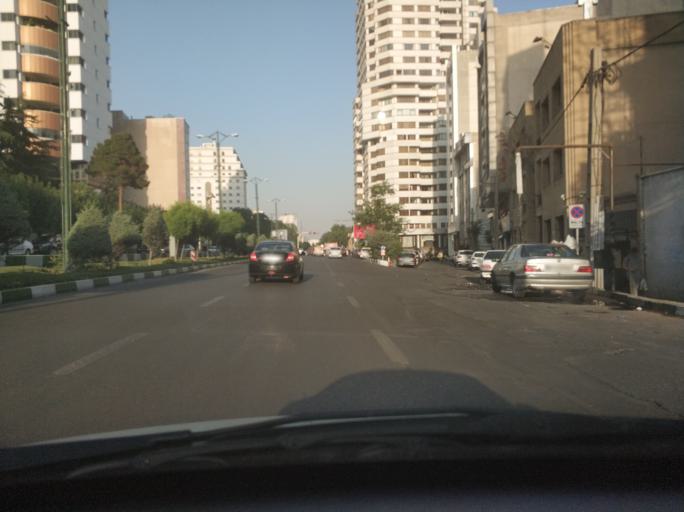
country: IR
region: Tehran
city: Tajrish
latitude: 35.8015
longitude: 51.4599
